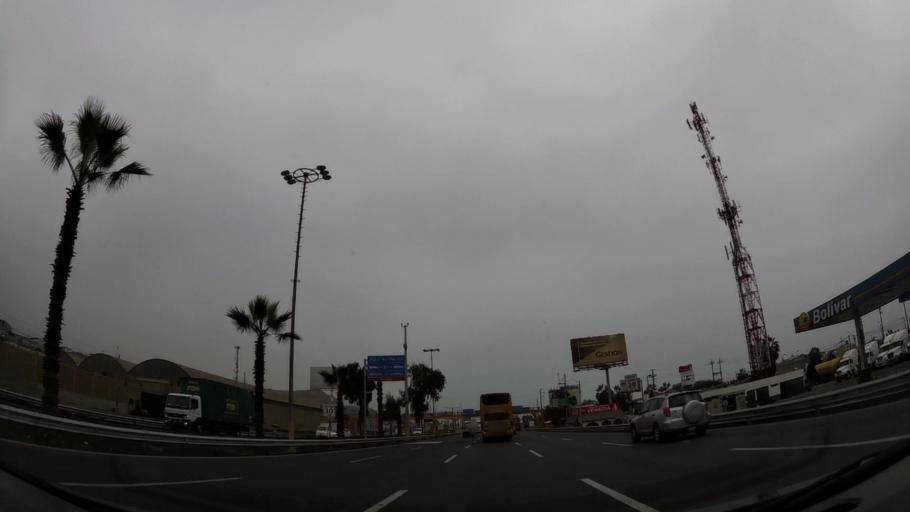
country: PE
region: Lima
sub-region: Lima
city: Surco
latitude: -12.2245
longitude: -76.9728
